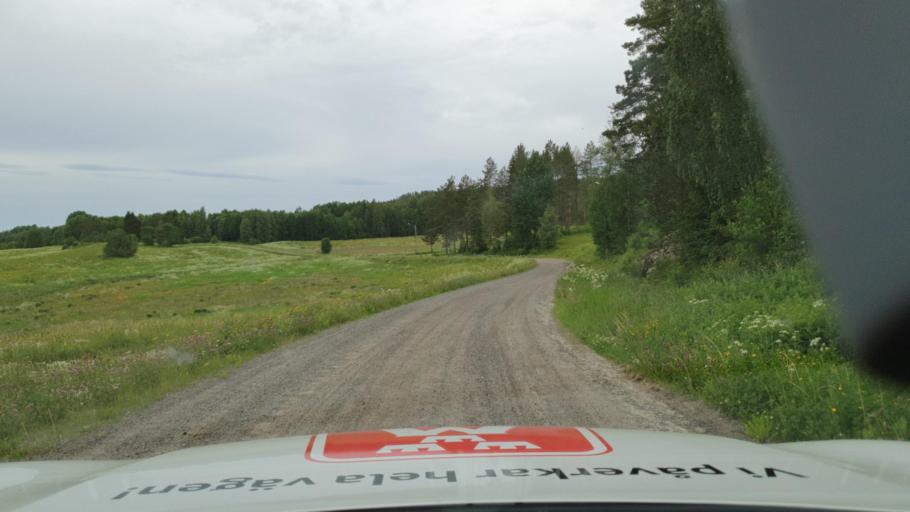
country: SE
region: Vaesterbotten
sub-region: Robertsfors Kommun
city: Robertsfors
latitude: 64.2027
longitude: 20.7013
